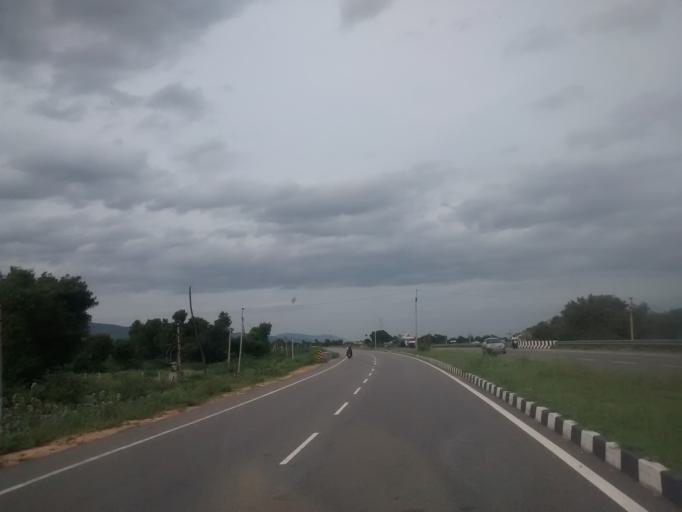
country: IN
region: Andhra Pradesh
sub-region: Chittoor
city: Narasingapuram
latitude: 13.5989
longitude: 79.3584
